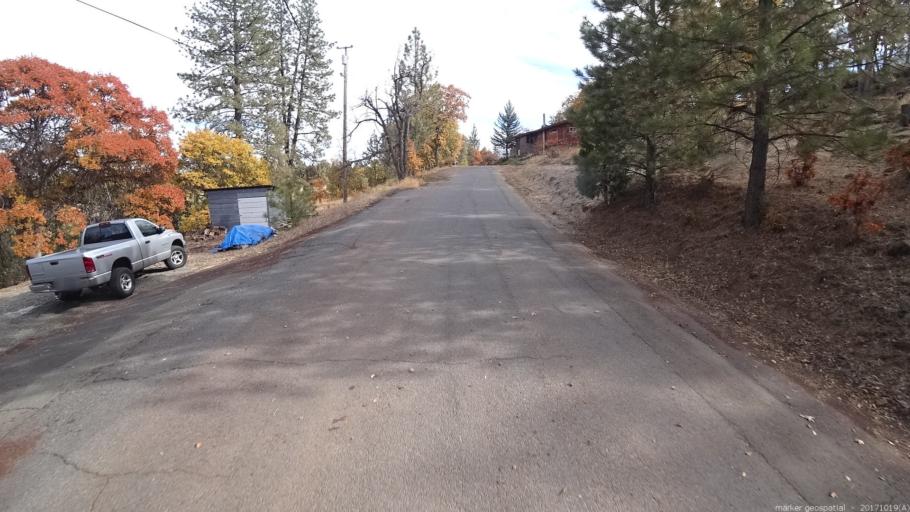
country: US
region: California
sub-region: Shasta County
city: Burney
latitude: 41.0002
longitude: -121.4394
